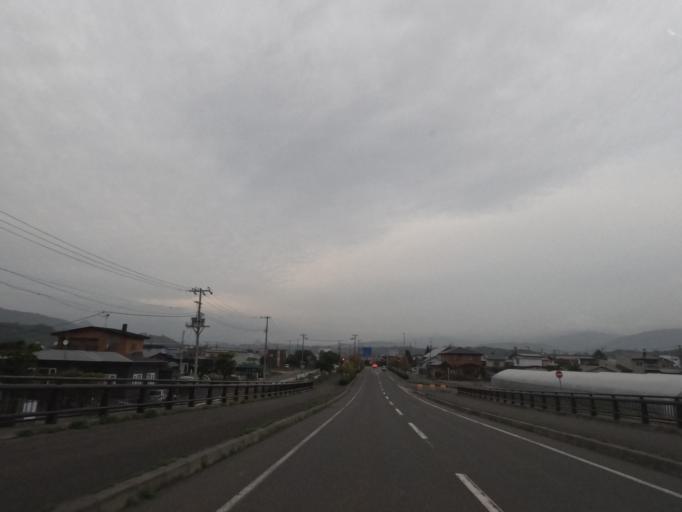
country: JP
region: Hokkaido
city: Date
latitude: 42.4900
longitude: 140.8331
